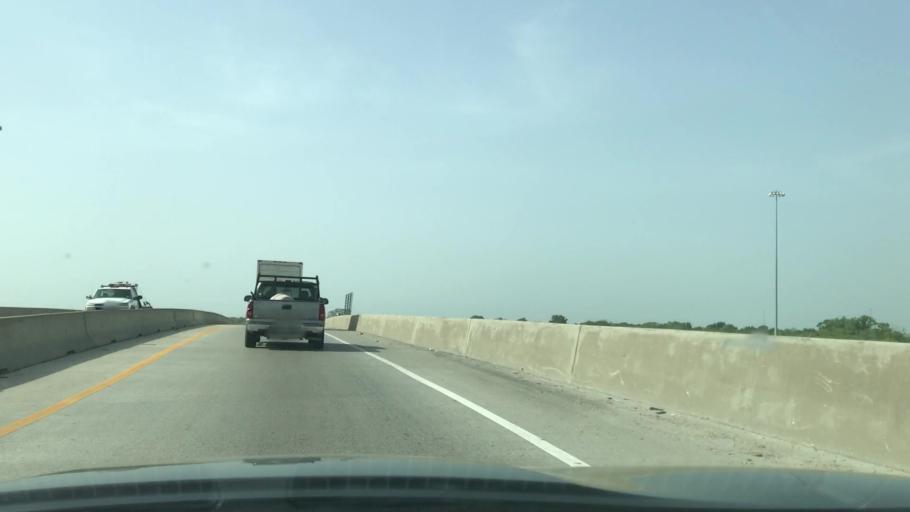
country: US
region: Texas
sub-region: Dallas County
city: Cockrell Hill
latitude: 32.7672
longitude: -96.9104
